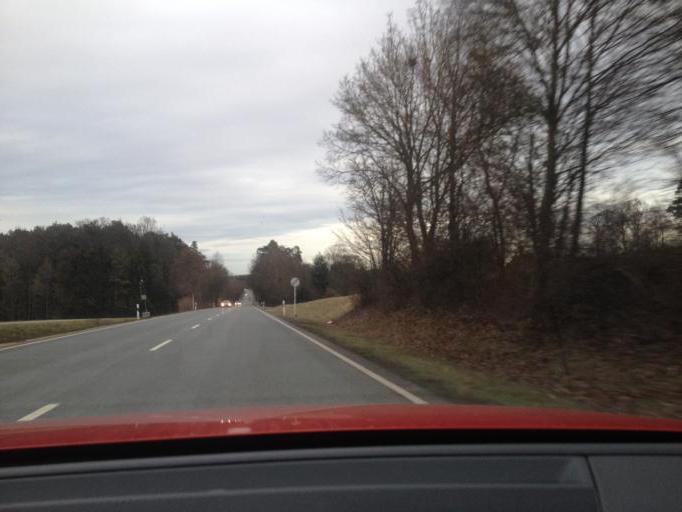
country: DE
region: Bavaria
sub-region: Regierungsbezirk Mittelfranken
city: Heilsbronn
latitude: 49.3506
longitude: 10.8330
